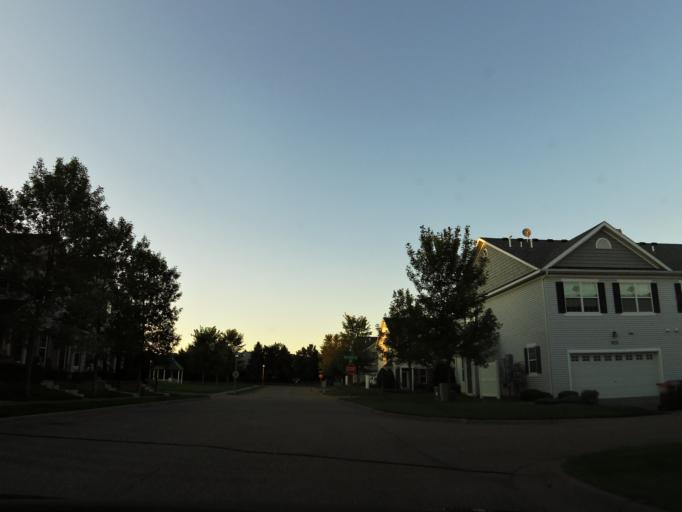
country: US
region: Minnesota
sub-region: Washington County
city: Oakdale
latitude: 44.9657
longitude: -92.9524
